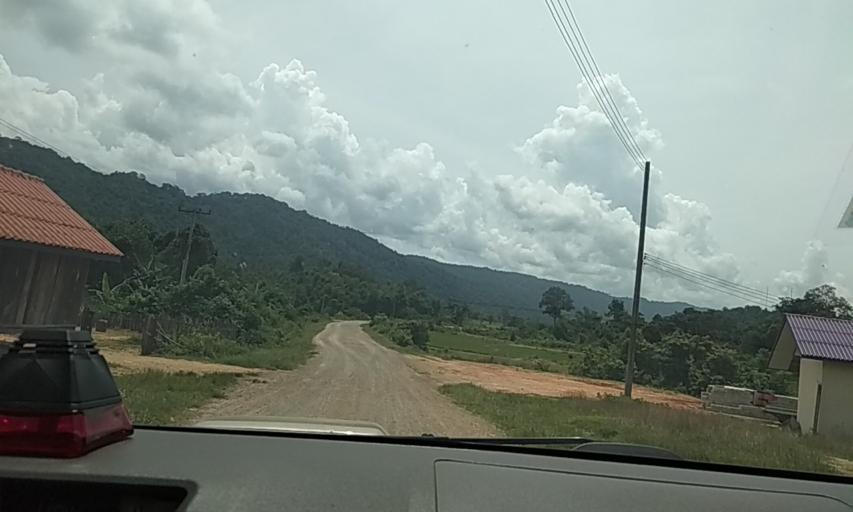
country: LA
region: Bolikhamxai
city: Ban Nahin
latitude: 18.1510
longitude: 104.7302
